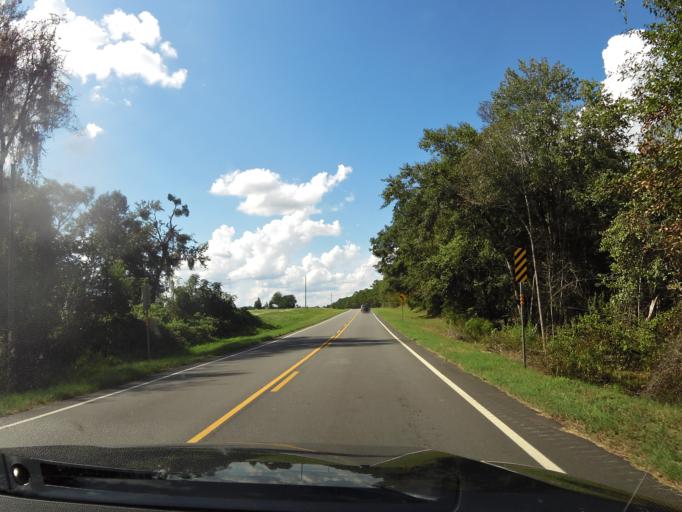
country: US
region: Georgia
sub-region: Echols County
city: Statenville
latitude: 30.7616
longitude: -83.1240
